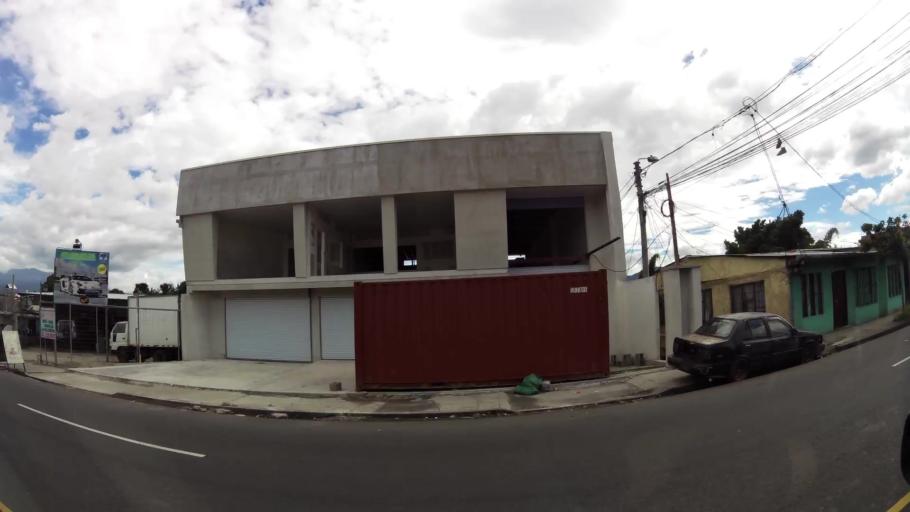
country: CR
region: San Jose
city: San Jose
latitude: 9.9195
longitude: -84.0837
